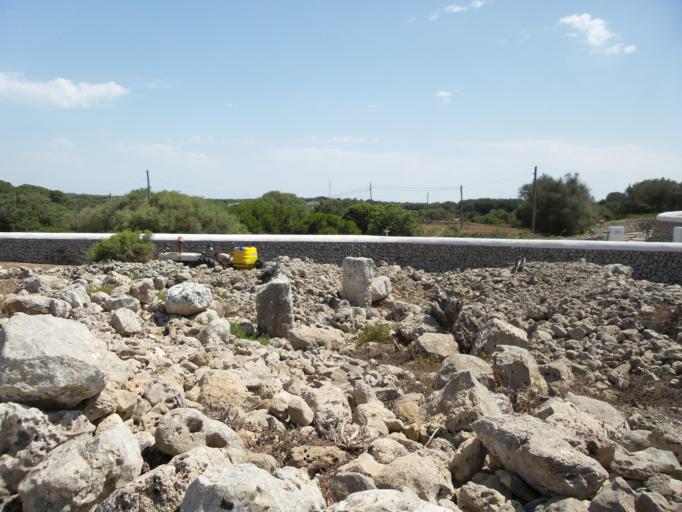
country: ES
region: Balearic Islands
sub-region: Illes Balears
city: Alaior
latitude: 39.9124
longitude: 4.1637
